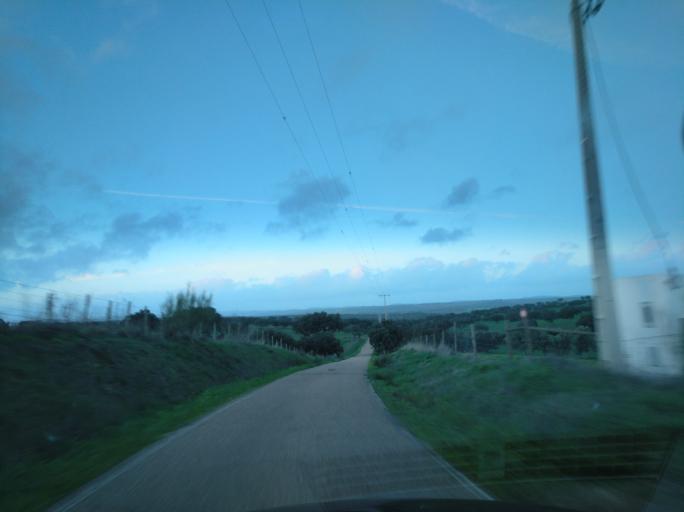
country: PT
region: Portalegre
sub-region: Campo Maior
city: Campo Maior
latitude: 39.0756
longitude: -7.1159
